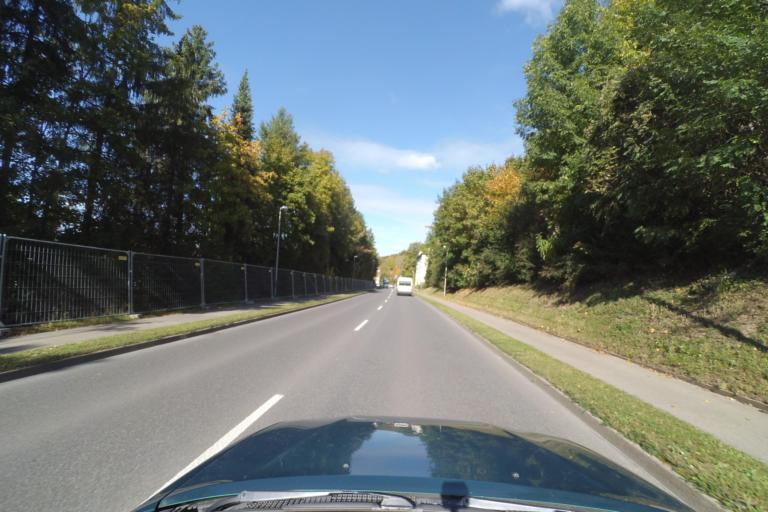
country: DE
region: Baden-Wuerttemberg
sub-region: Karlsruhe Region
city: Nagold
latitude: 48.5420
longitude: 8.7306
